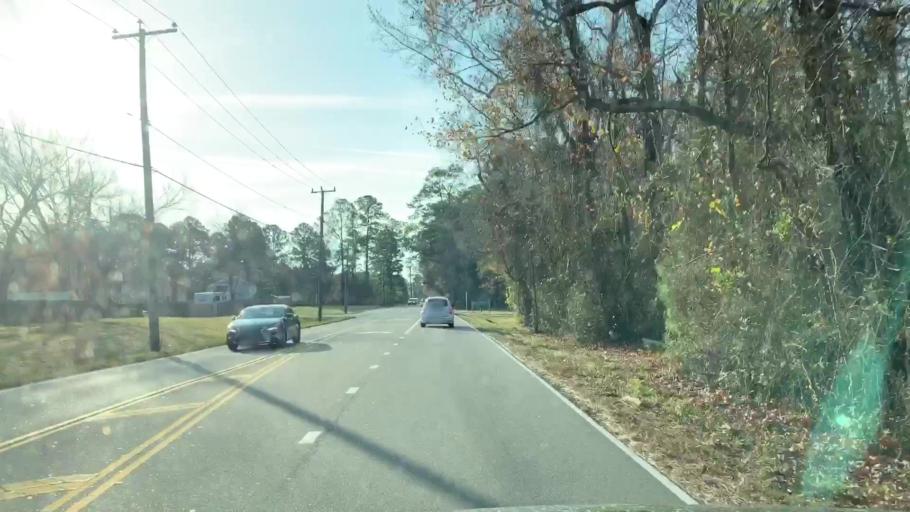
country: US
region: Virginia
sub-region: City of Chesapeake
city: Chesapeake
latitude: 36.7770
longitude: -76.1567
